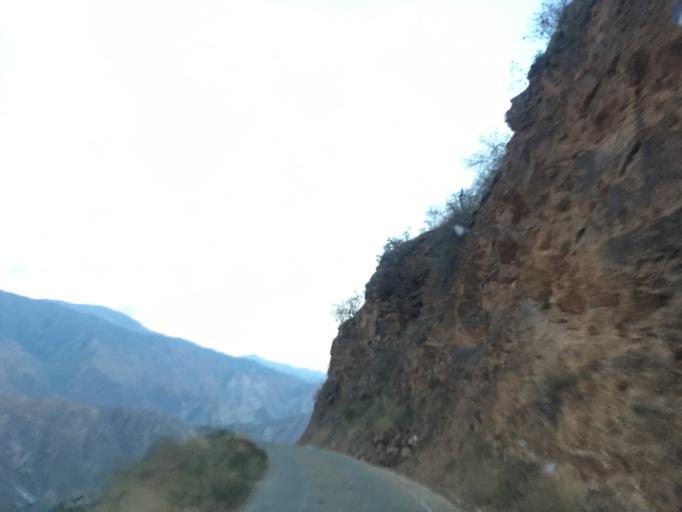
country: CO
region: Santander
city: Aratoca
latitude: 6.7887
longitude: -72.9962
